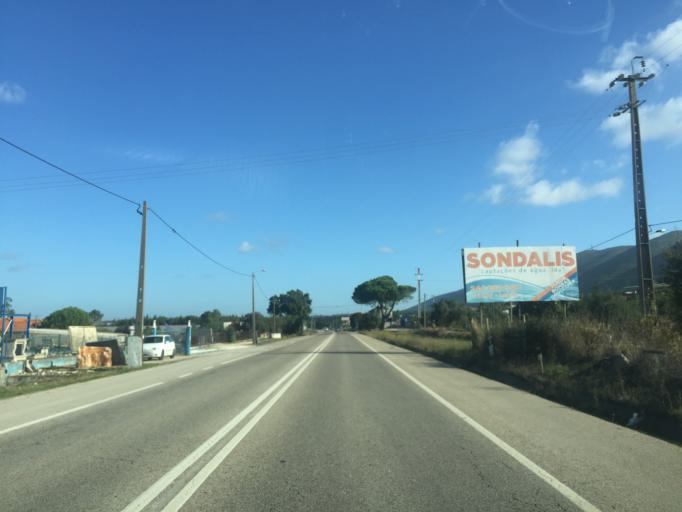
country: PT
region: Leiria
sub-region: Alcobaca
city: Aljubarrota
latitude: 39.5283
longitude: -8.9081
